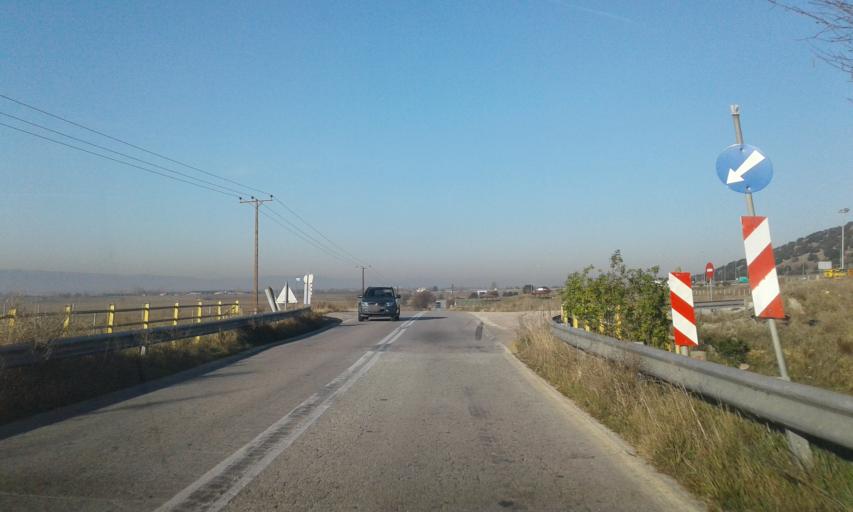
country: GR
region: Central Macedonia
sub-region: Nomos Thessalonikis
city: Kolchikon
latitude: 40.7056
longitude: 23.1925
